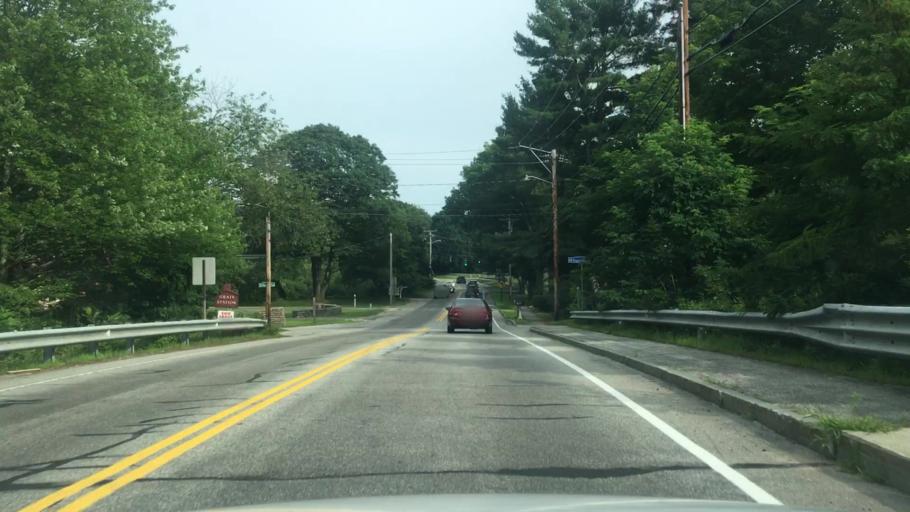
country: US
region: Maine
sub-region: York County
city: Kennebunk
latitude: 43.3834
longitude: -70.5284
